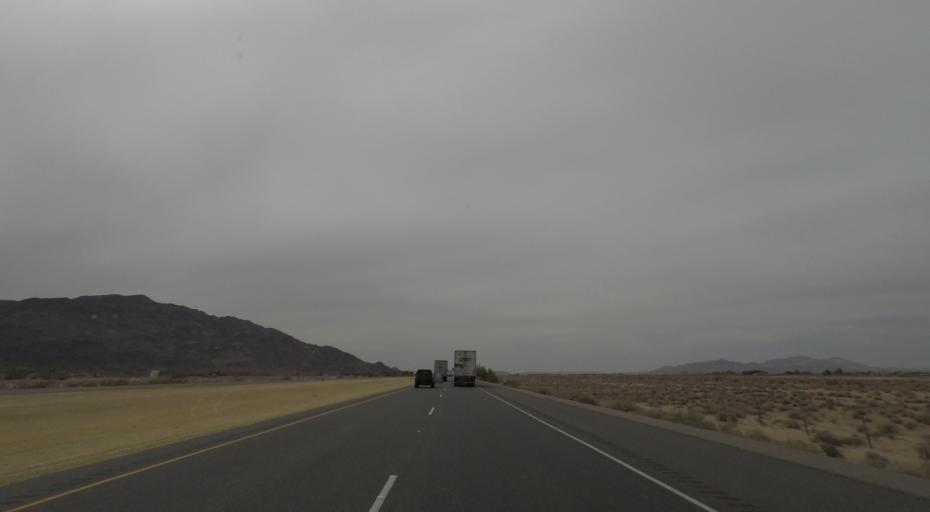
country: US
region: California
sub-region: San Bernardino County
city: Barstow
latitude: 34.8220
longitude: -116.6408
